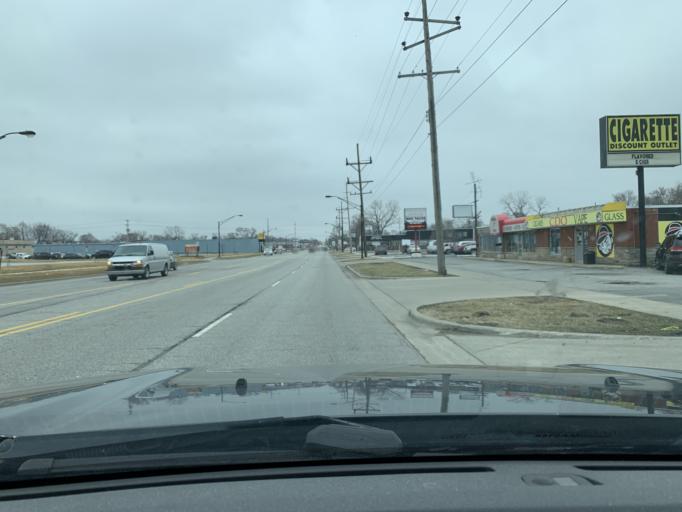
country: US
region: Indiana
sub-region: Lake County
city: Highland
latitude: 41.5684
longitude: -87.4617
